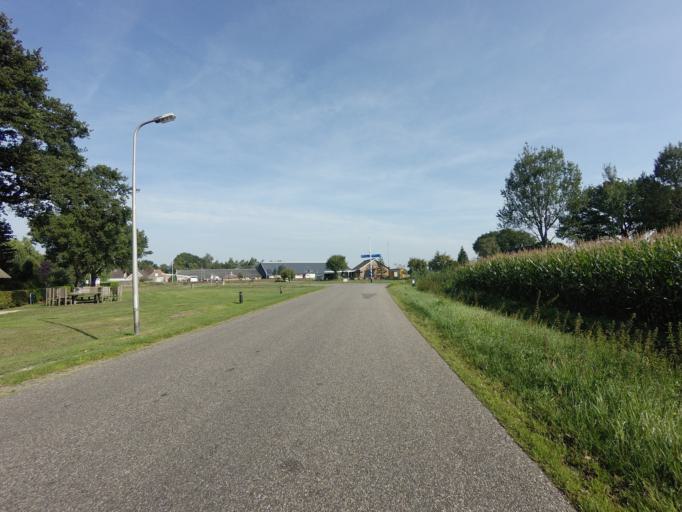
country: DE
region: Lower Saxony
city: Wielen
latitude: 52.5639
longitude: 6.6699
